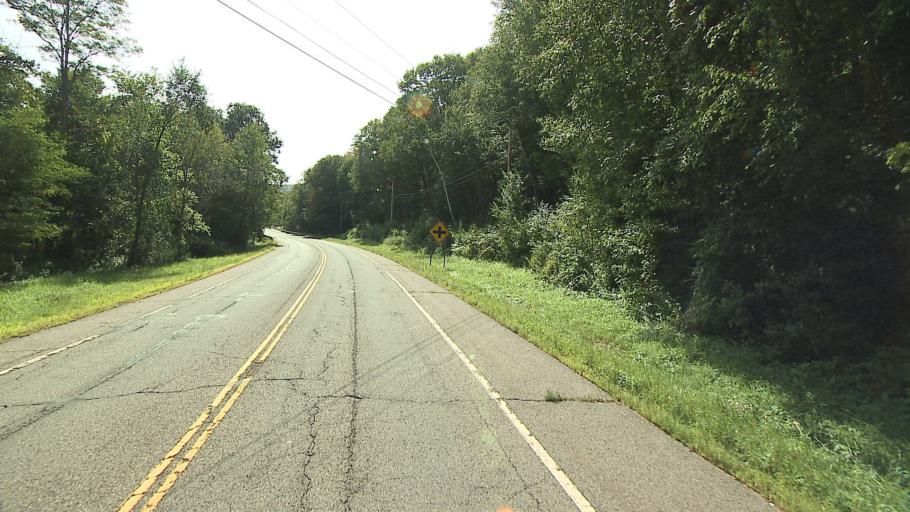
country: US
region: Connecticut
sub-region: Litchfield County
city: Thomaston
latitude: 41.6754
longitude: -73.0902
